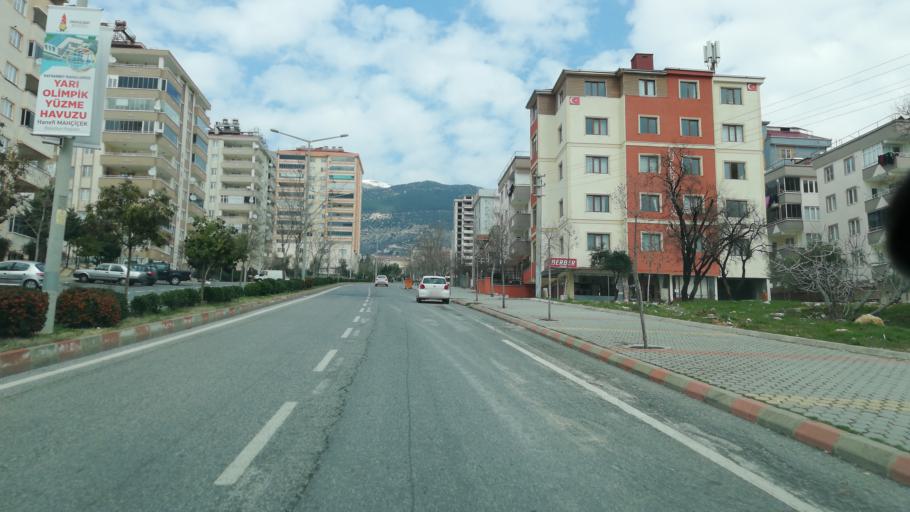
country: TR
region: Kahramanmaras
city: Kahramanmaras
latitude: 37.5901
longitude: 36.8633
